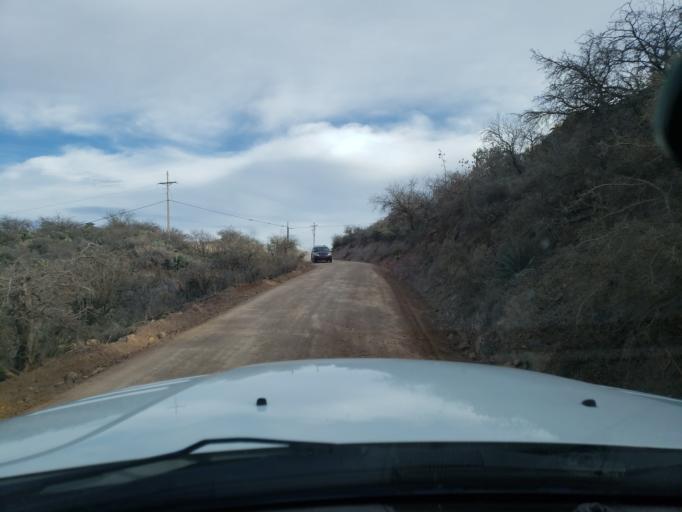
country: US
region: Arizona
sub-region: Pinal County
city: Oracle
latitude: 32.5485
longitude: -110.7061
